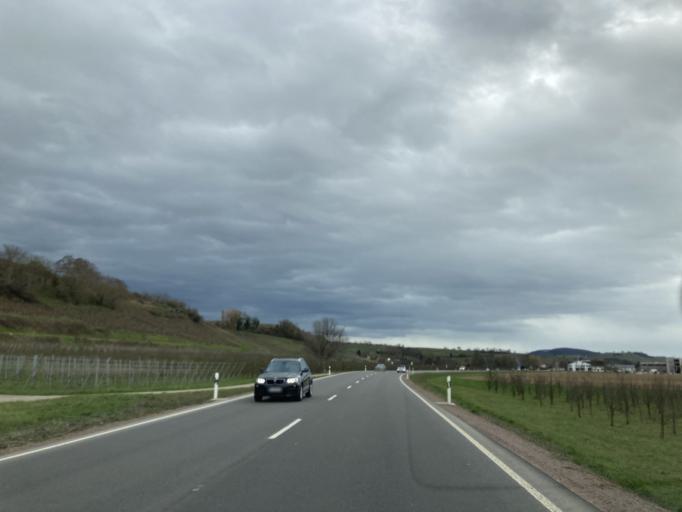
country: DE
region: Baden-Wuerttemberg
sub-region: Freiburg Region
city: Buggingen
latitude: 47.8386
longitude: 7.6227
